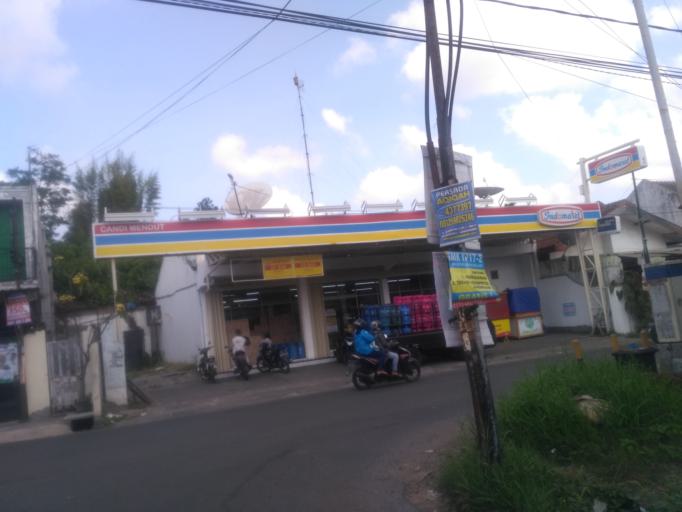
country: ID
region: East Java
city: Malang
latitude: -7.9442
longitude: 112.6346
